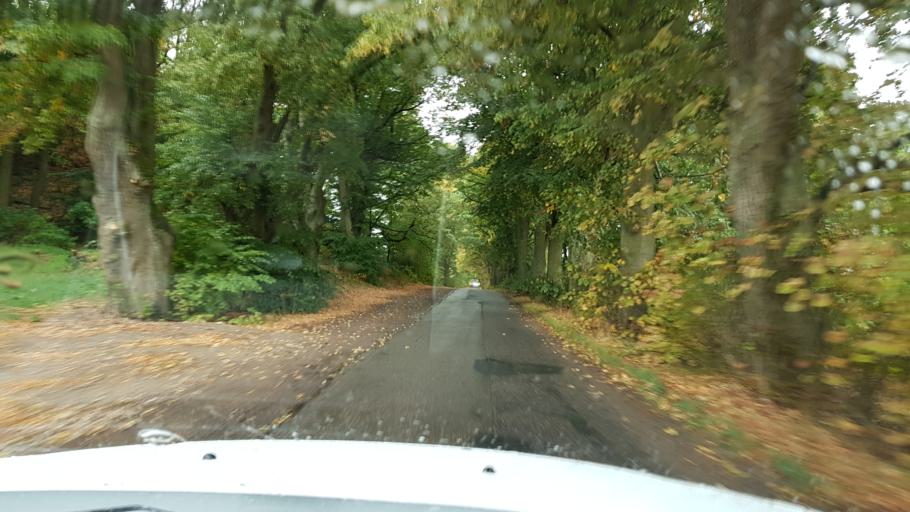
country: DE
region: Brandenburg
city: Schwedt (Oder)
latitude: 53.0055
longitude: 14.2923
